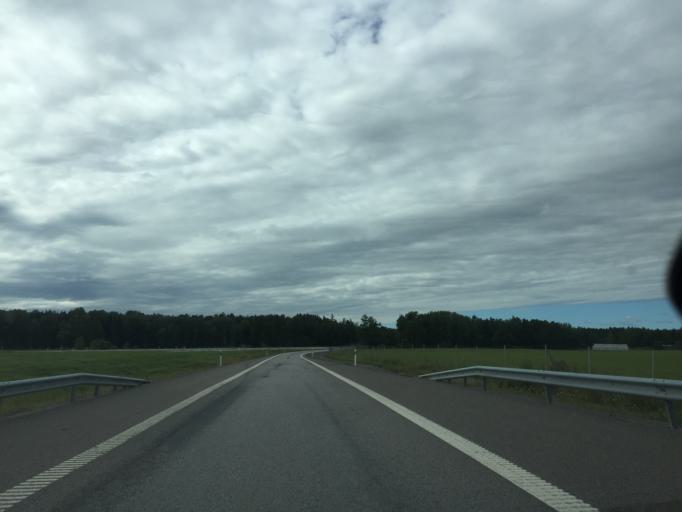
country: SE
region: Vaestmanland
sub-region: Arboga Kommun
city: Arboga
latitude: 59.4284
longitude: 15.8806
